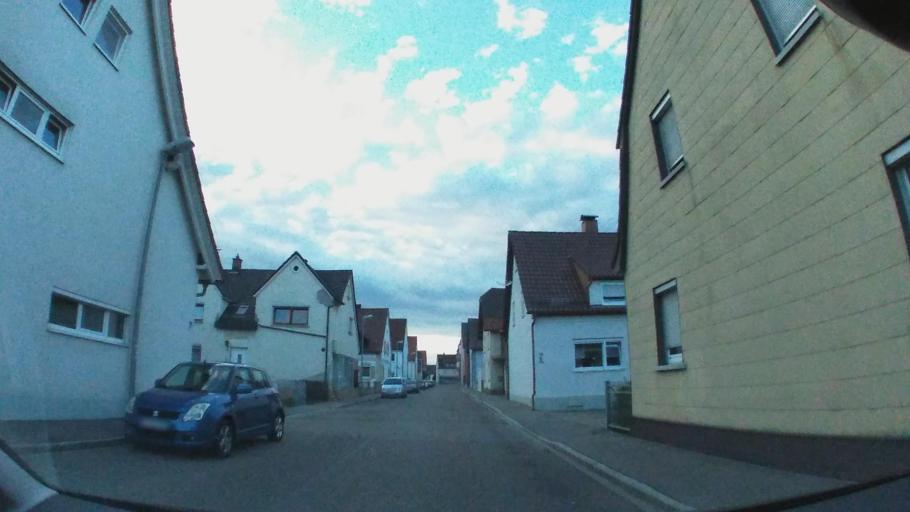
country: DE
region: Bavaria
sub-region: Swabia
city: Neu-Ulm
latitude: 48.4047
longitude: 10.0329
